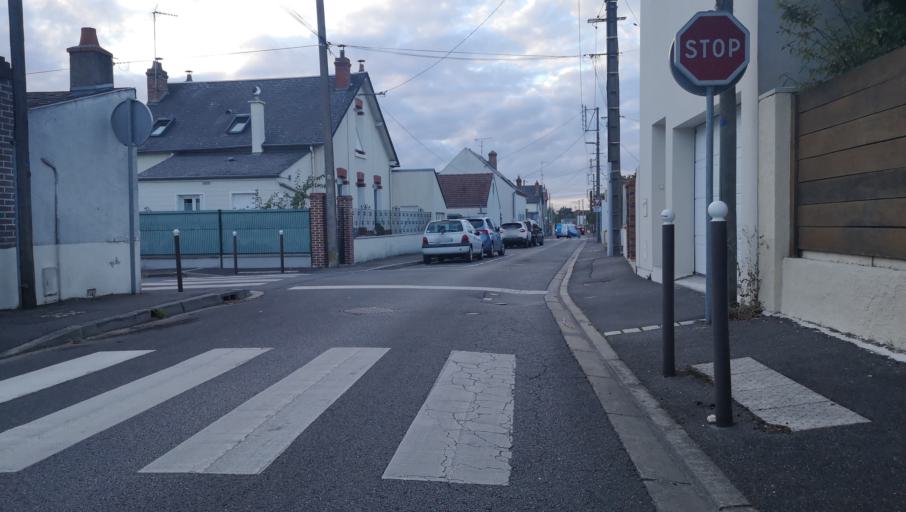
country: FR
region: Centre
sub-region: Departement du Loiret
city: Saint-Jean-de-la-Ruelle
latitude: 47.9050
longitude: 1.8827
